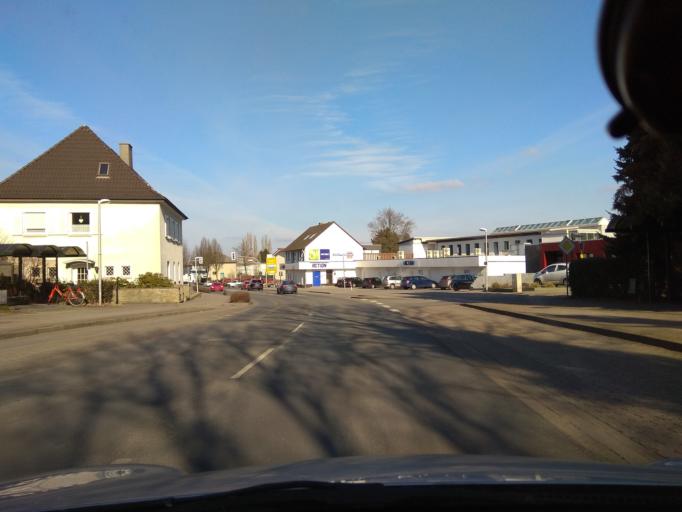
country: DE
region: North Rhine-Westphalia
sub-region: Regierungsbezirk Munster
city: Mettingen
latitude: 52.3138
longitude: 7.7839
